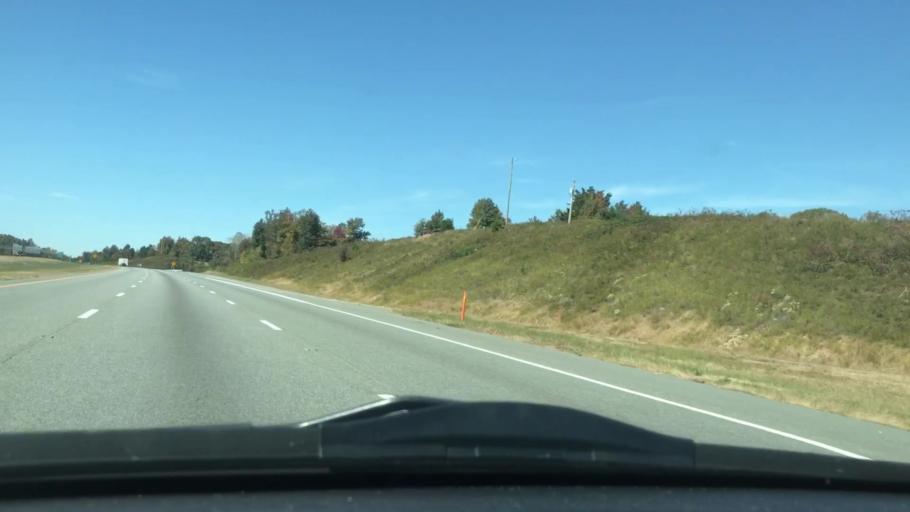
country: US
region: North Carolina
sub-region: Randolph County
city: Archdale
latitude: 35.9313
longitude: -79.9260
